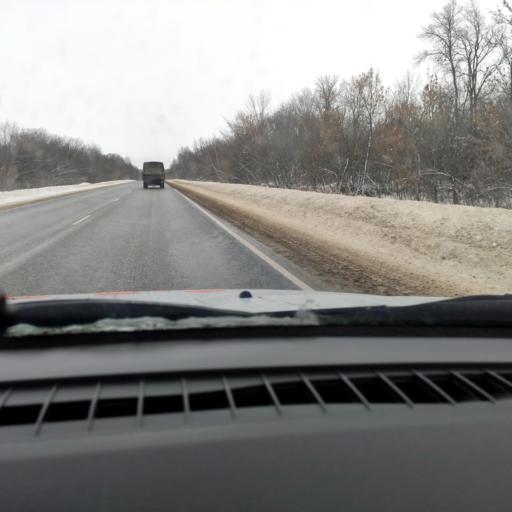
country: RU
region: Samara
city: Dubovyy Umet
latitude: 52.9572
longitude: 50.2996
